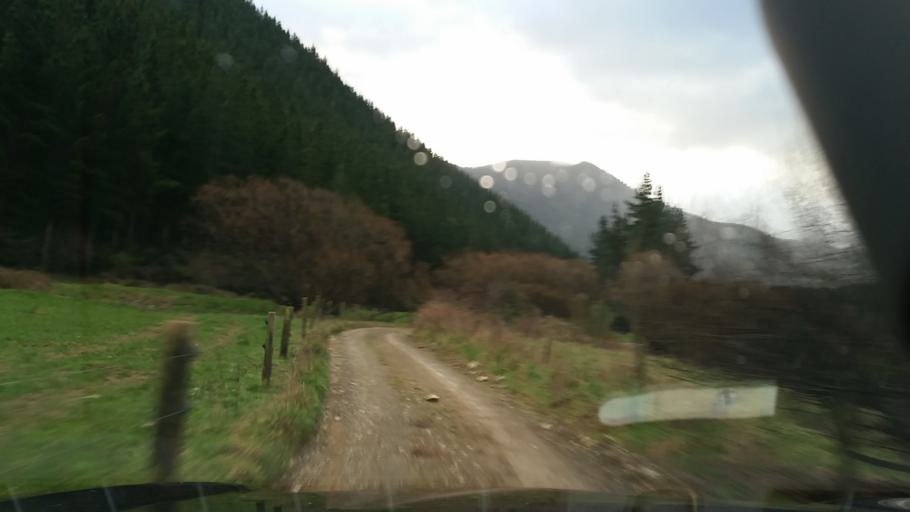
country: NZ
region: Marlborough
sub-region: Marlborough District
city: Picton
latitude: -41.2148
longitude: 173.6965
